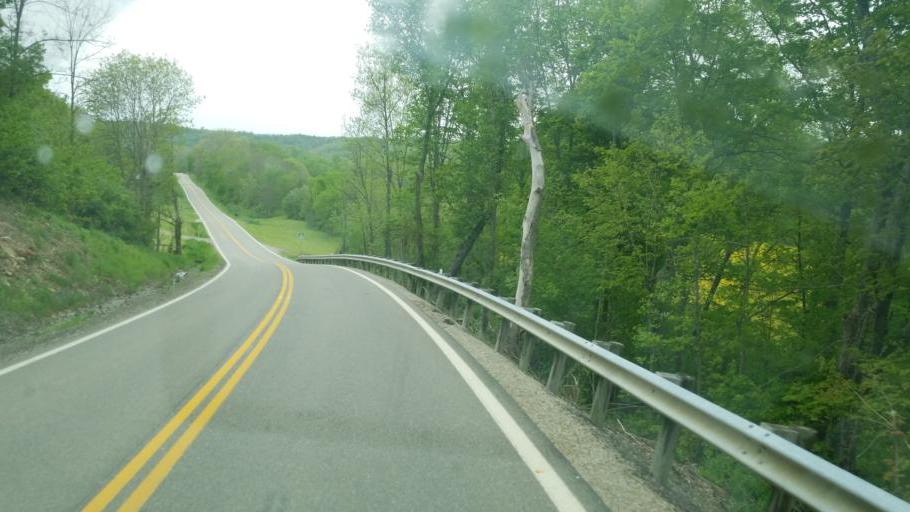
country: US
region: Ohio
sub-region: Guernsey County
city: Mantua
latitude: 40.1579
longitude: -81.6055
